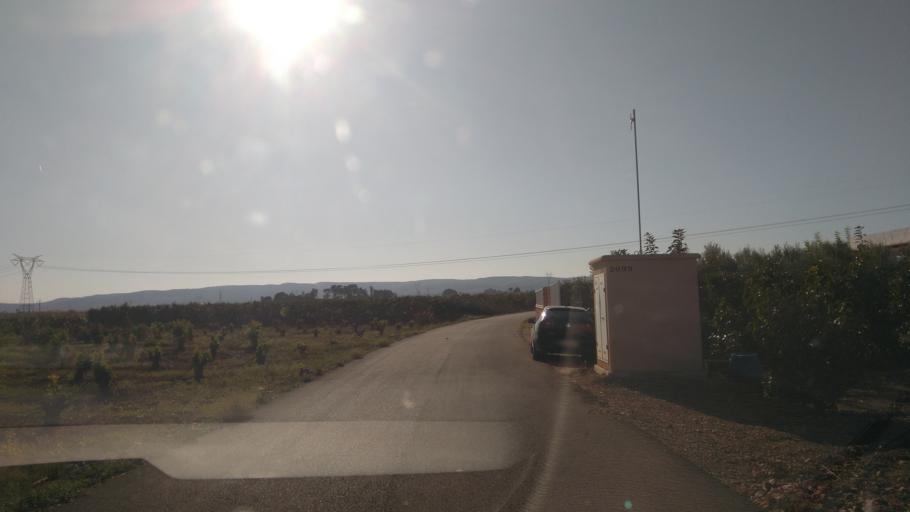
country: ES
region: Valencia
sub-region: Provincia de Valencia
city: Masalaves
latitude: 39.1773
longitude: -0.5397
